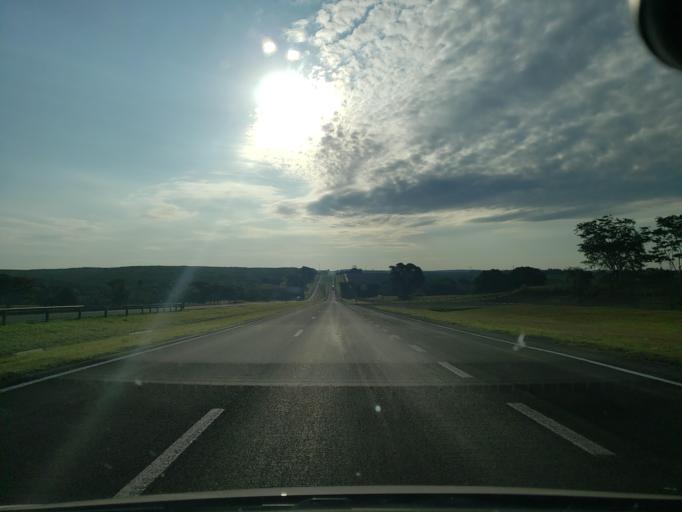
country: BR
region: Sao Paulo
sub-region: Valparaiso
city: Valparaiso
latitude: -21.1901
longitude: -50.9092
